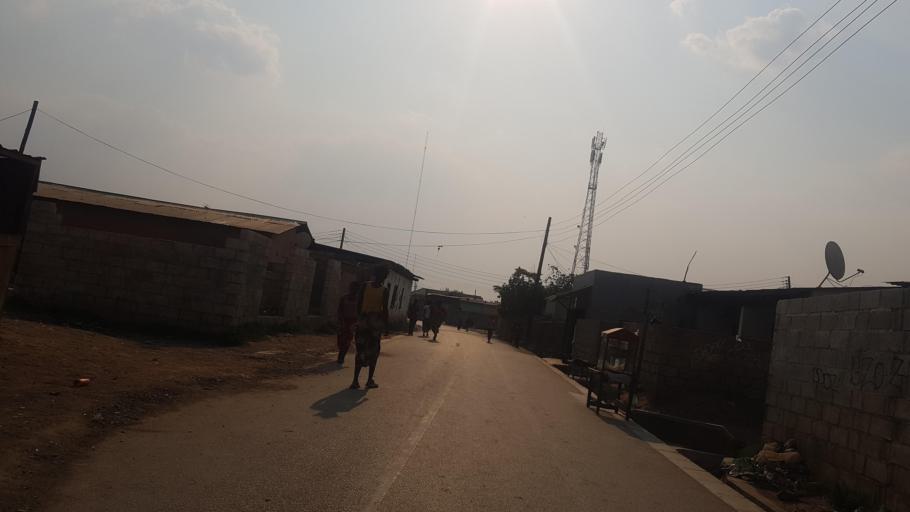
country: ZM
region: Lusaka
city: Lusaka
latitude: -15.4437
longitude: 28.3825
